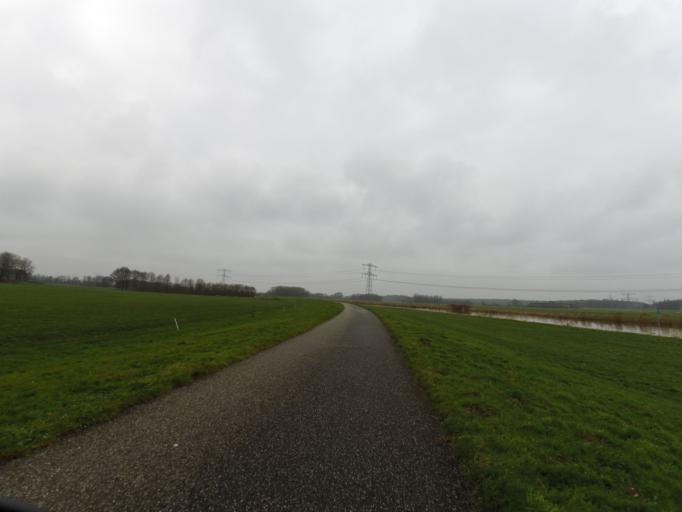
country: NL
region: Gelderland
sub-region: Gemeente Doetinchem
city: Doetinchem
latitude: 51.9790
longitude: 6.2424
